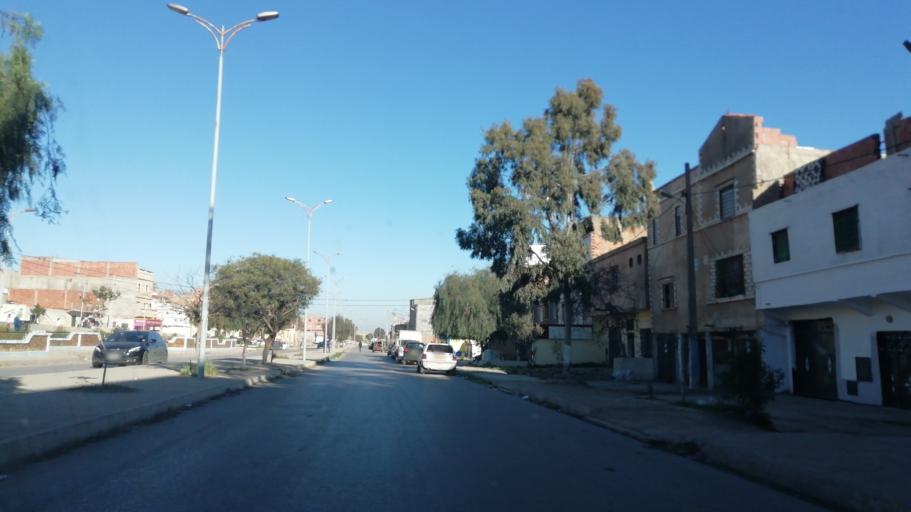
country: DZ
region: Oran
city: Bir el Djir
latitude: 35.7203
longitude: -0.5425
